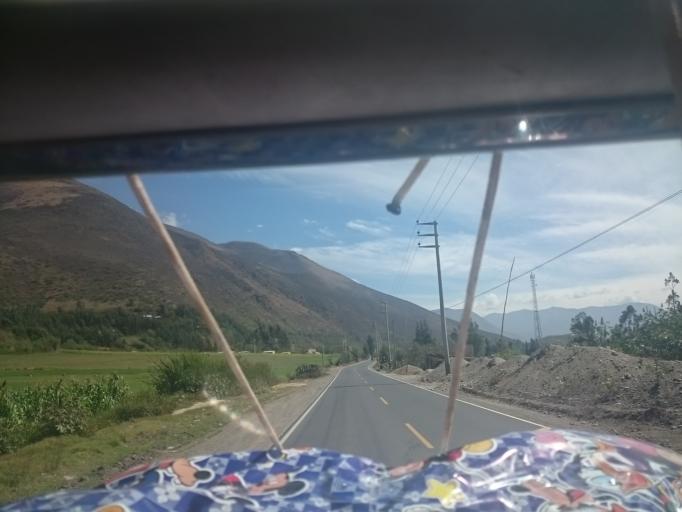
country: PE
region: Huanuco
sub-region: Provincia de Ambo
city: Conchamarca
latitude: -10.0414
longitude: -76.2290
